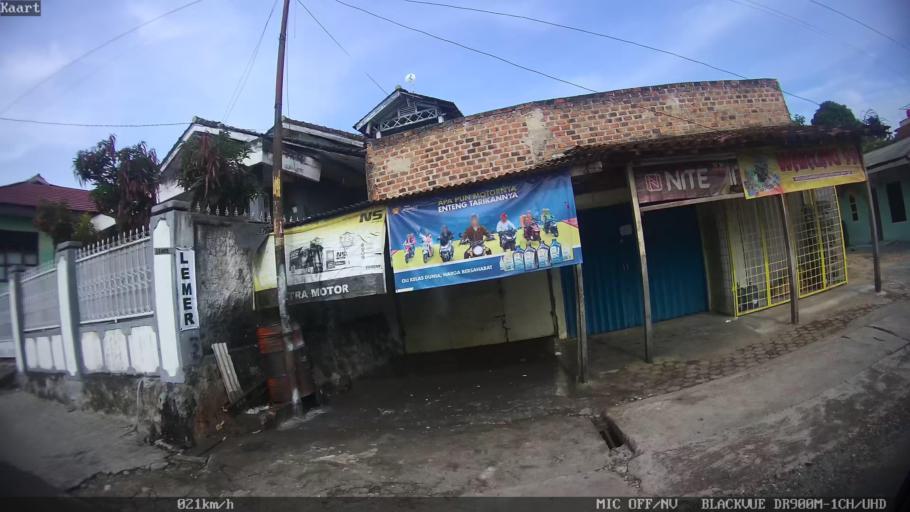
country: ID
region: Lampung
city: Kedaton
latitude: -5.3951
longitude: 105.2660
